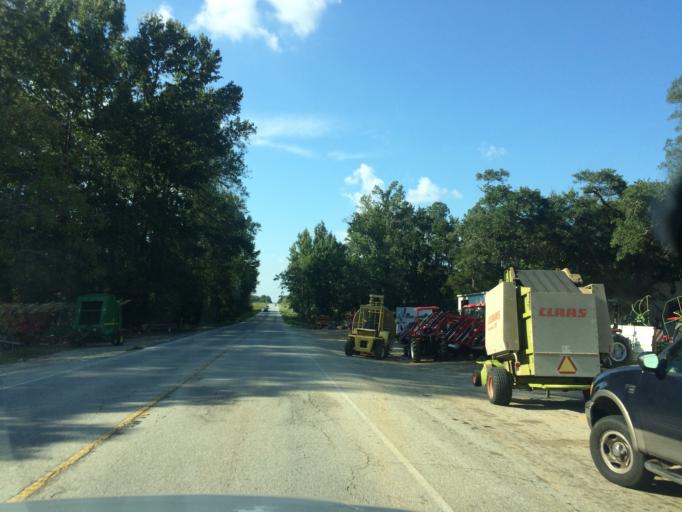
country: US
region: South Carolina
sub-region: Laurens County
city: Laurens
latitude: 34.5439
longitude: -82.0686
